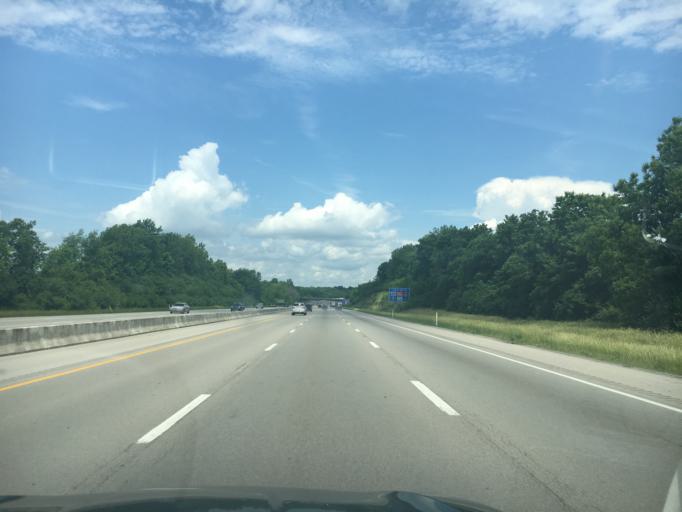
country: US
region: Kentucky
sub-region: Fayette County
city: Lexington
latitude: 37.9449
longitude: -84.3828
